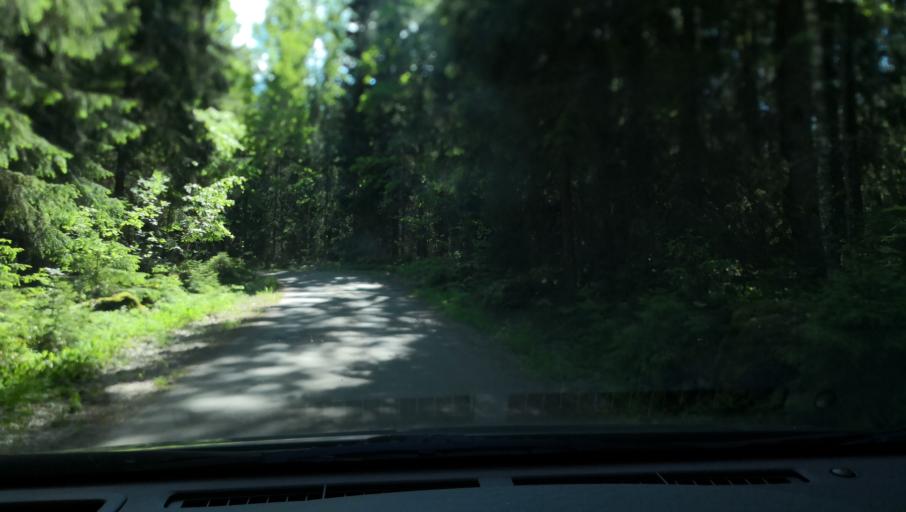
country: SE
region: Vaestmanland
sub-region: Arboga Kommun
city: Tyringe
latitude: 59.3184
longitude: 15.9963
